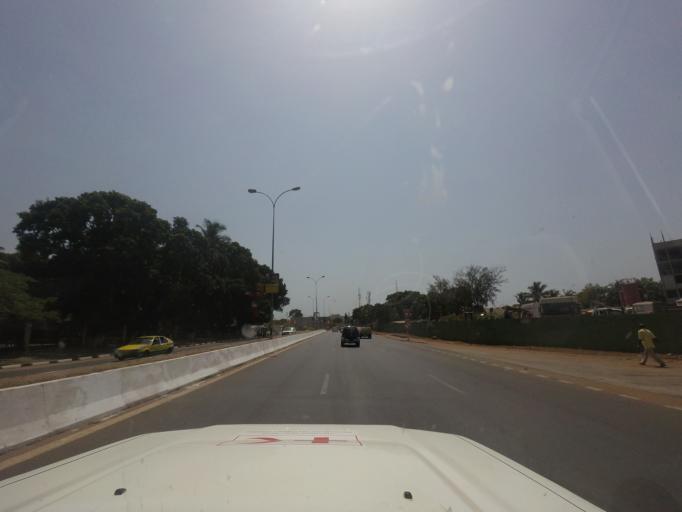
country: GN
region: Conakry
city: Camayenne
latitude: 9.5207
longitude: -13.6936
